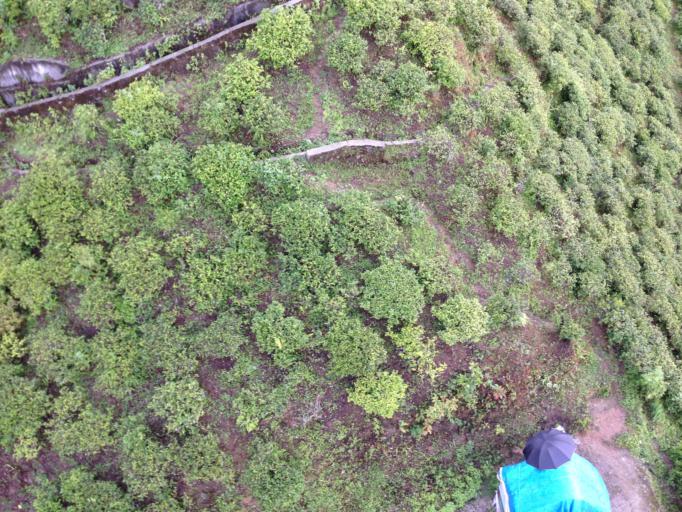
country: IN
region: West Bengal
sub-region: Darjiling
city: Darjiling
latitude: 27.0659
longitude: 88.2544
